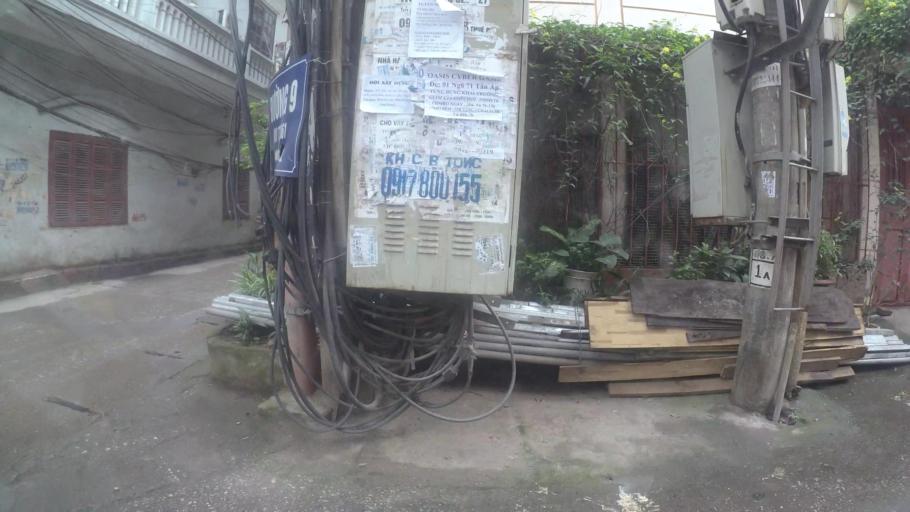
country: VN
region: Ha Noi
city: Hoan Kiem
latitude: 21.0498
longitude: 105.8440
